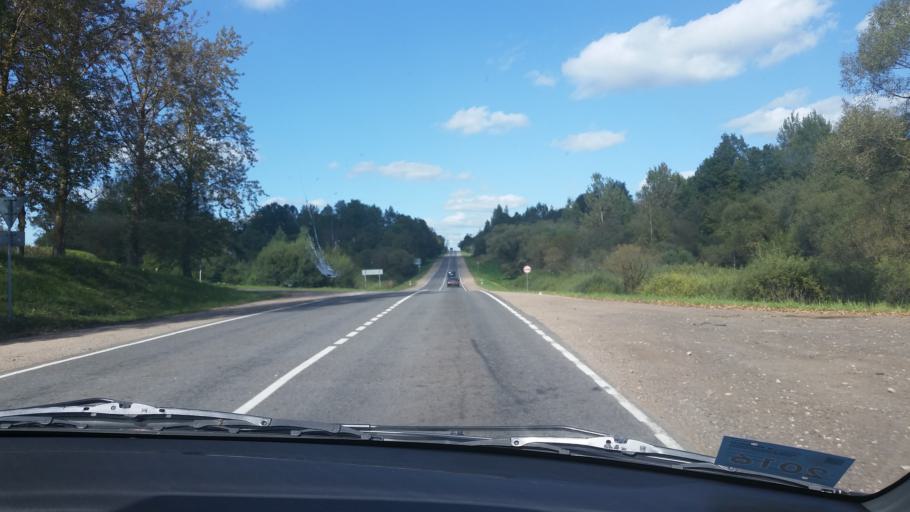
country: BY
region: Vitebsk
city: Vitebsk
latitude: 55.1049
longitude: 30.2842
